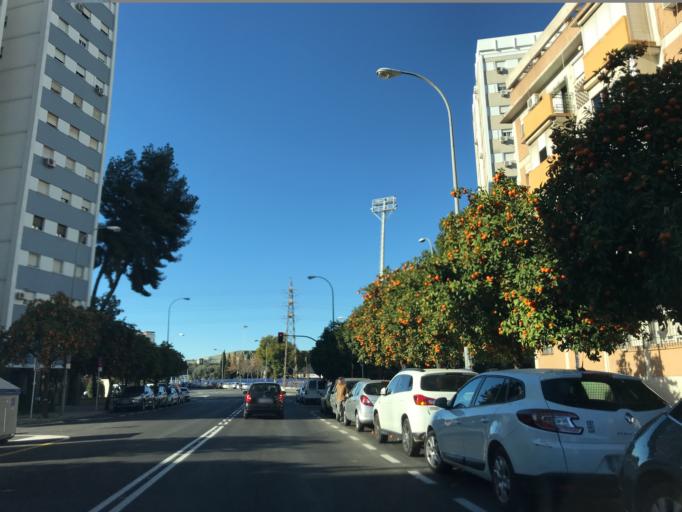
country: ES
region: Andalusia
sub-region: Provincia de Sevilla
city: Sevilla
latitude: 37.3983
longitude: -5.9603
